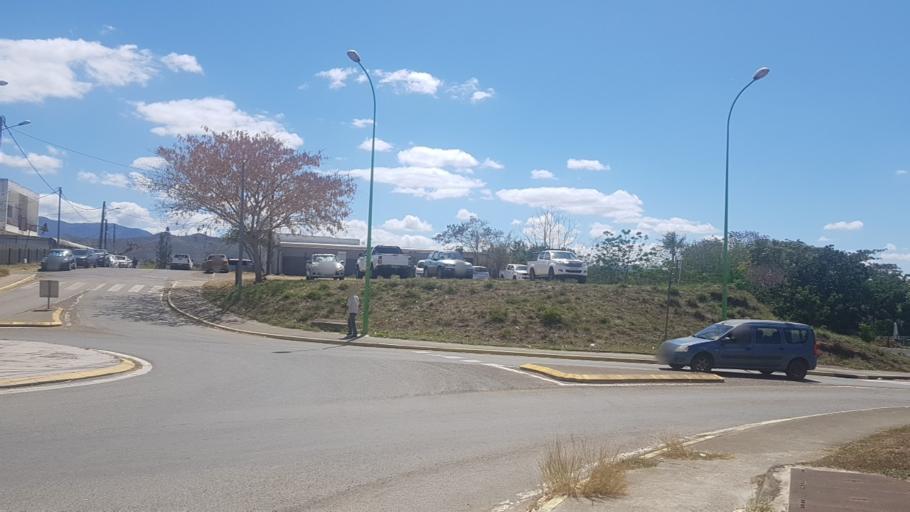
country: NC
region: North Province
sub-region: Kone
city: Kone
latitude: -21.0617
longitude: 164.8619
